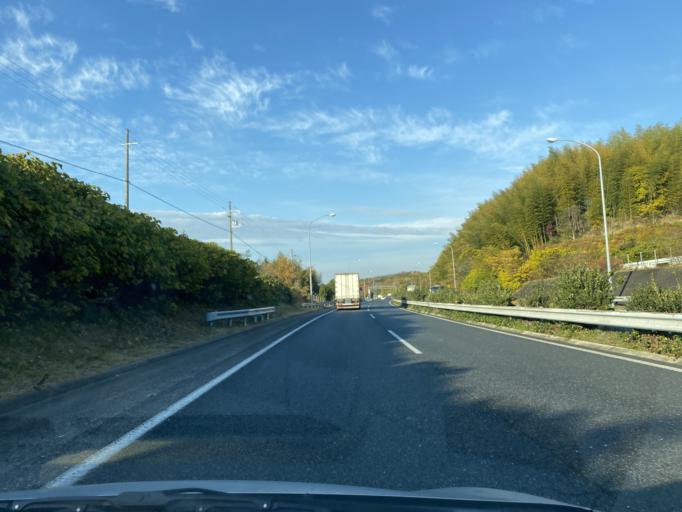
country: JP
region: Osaka
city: Izumi
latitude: 34.4199
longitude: 135.4479
